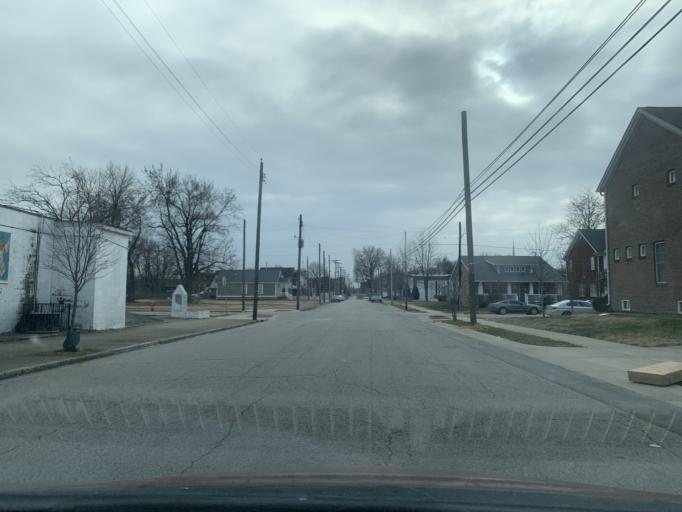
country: US
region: Kentucky
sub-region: Jefferson County
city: Louisville
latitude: 38.2557
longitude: -85.7820
